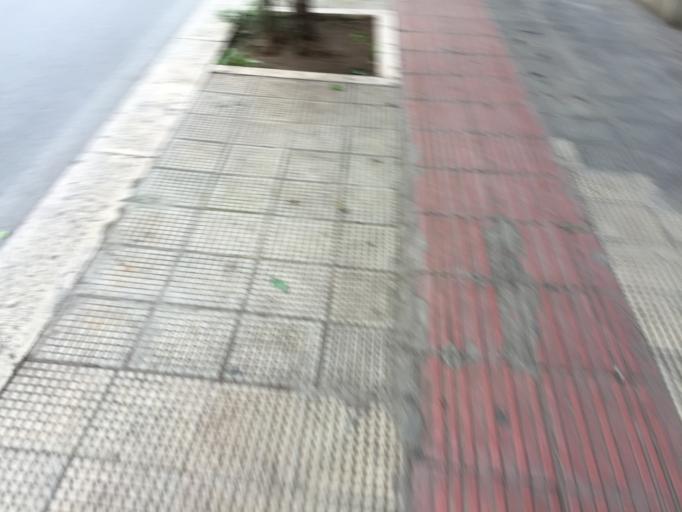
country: IT
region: Apulia
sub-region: Provincia di Bari
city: Bari
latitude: 41.1202
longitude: 16.8656
